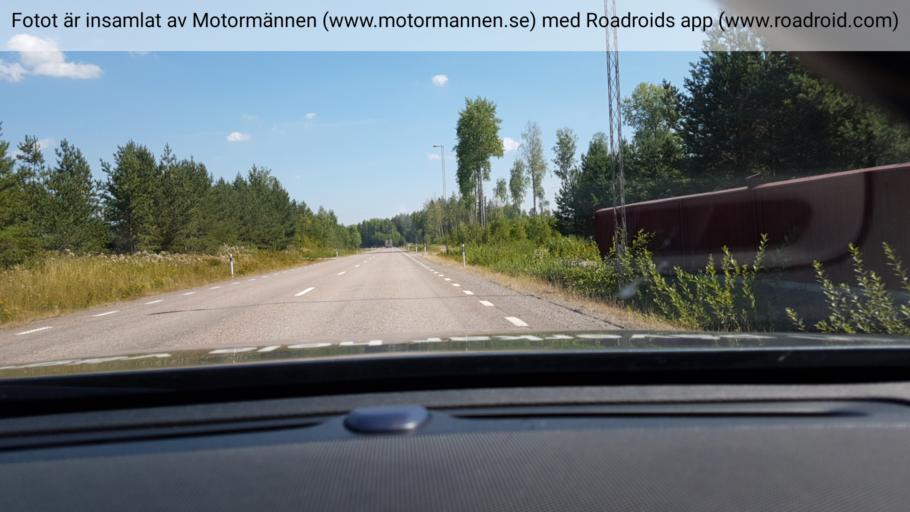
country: SE
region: Dalarna
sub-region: Avesta Kommun
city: Horndal
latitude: 60.2620
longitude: 16.3793
